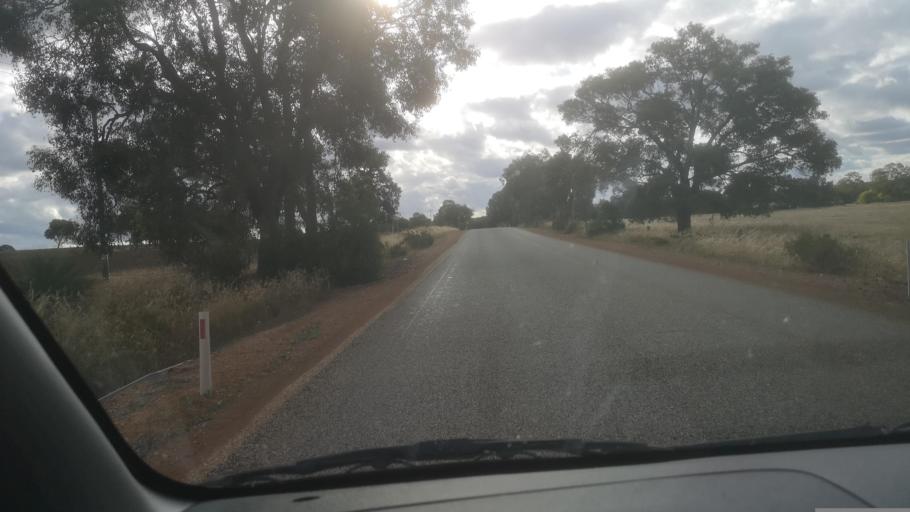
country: AU
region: Western Australia
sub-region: Chittering
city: Lower Chittering
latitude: -31.3273
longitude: 116.0314
